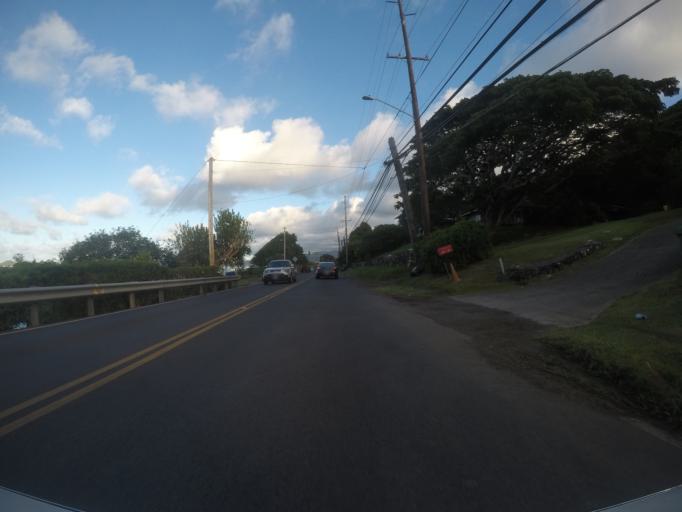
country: US
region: Hawaii
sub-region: Honolulu County
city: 'Ahuimanu
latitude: 21.4535
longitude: -157.8161
